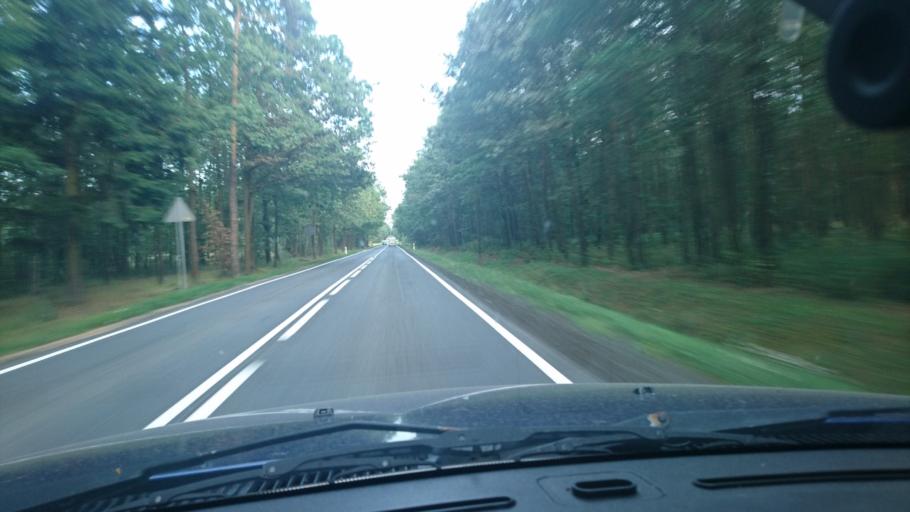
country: PL
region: Opole Voivodeship
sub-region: Powiat oleski
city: Olesno
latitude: 50.8492
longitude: 18.4732
